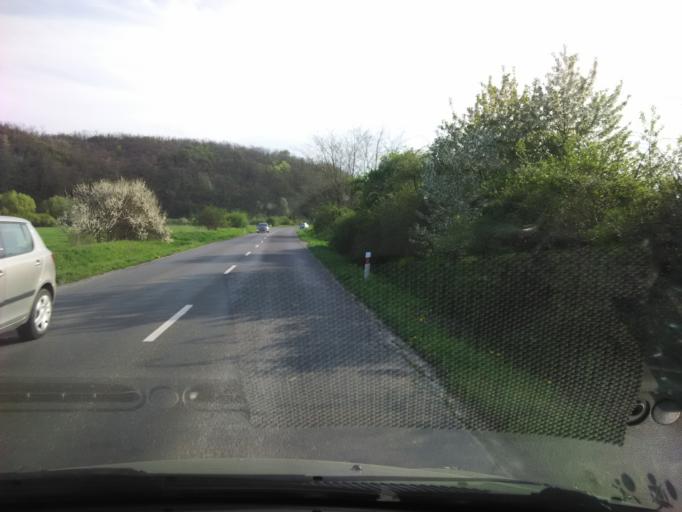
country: SK
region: Nitriansky
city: Levice
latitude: 48.2444
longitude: 18.6007
